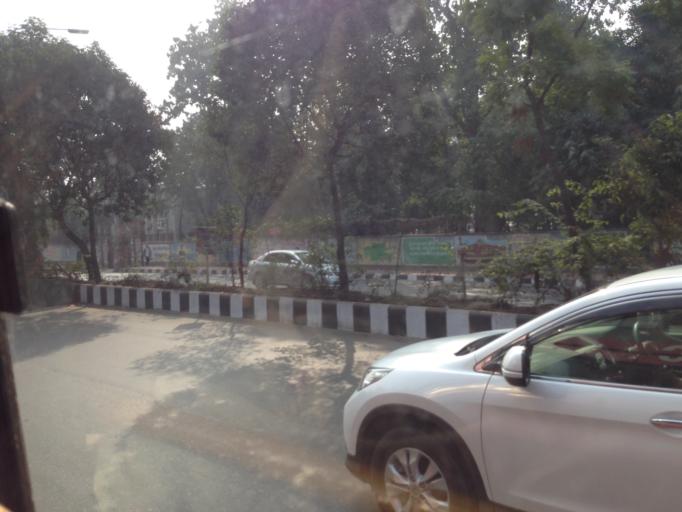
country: BD
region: Dhaka
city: Azimpur
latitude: 23.7669
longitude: 90.3696
